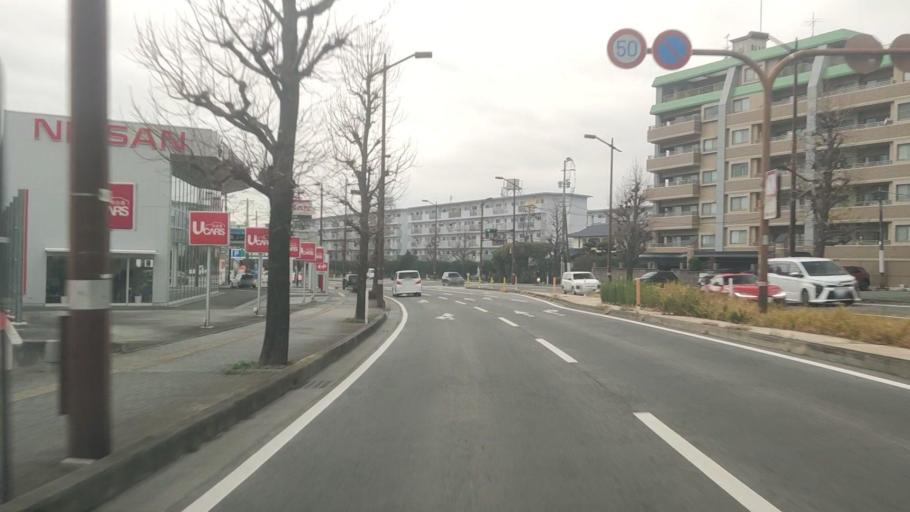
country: JP
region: Kumamoto
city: Kumamoto
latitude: 32.8117
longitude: 130.7752
